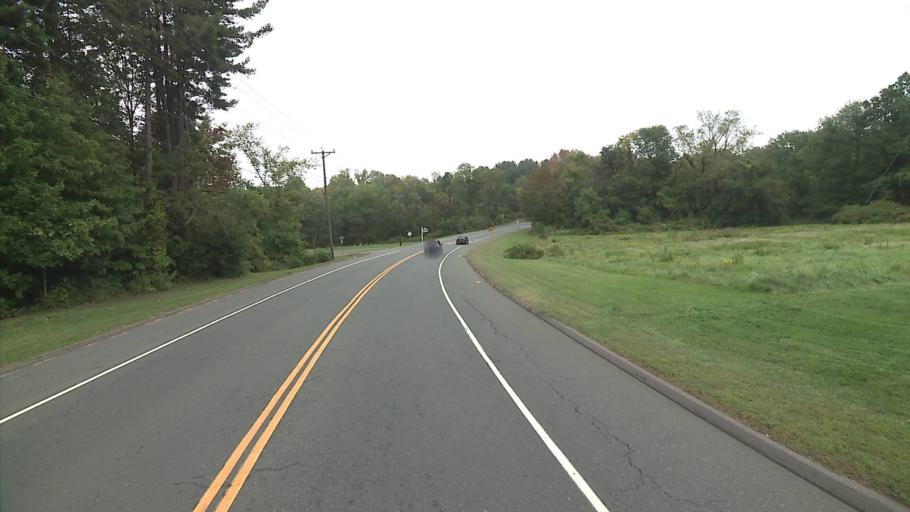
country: US
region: Connecticut
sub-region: Hartford County
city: Suffield Depot
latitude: 41.9722
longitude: -72.6595
